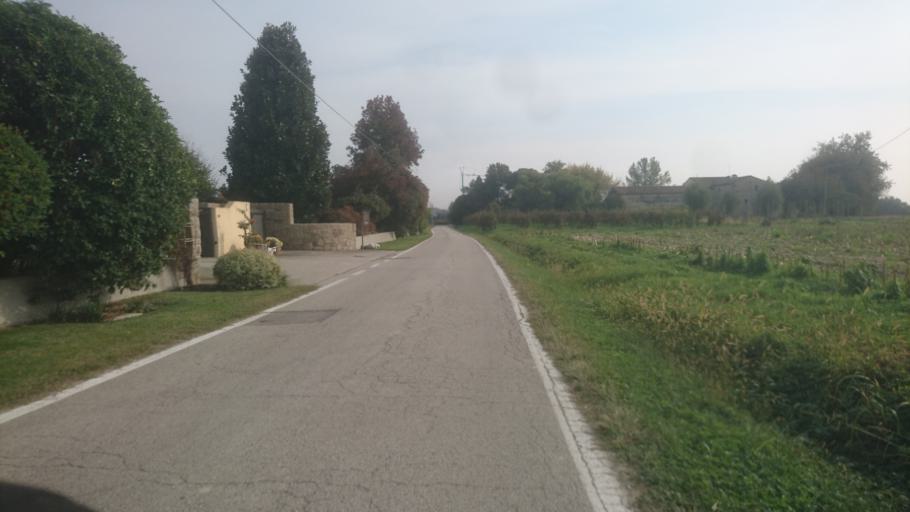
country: IT
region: Veneto
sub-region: Provincia di Vicenza
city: Montegalda
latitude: 45.4691
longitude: 11.6497
